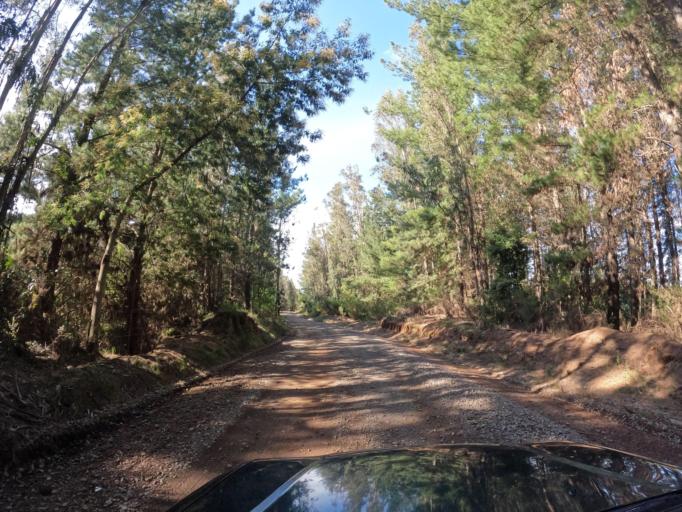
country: CL
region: Biobio
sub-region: Provincia de Biobio
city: La Laja
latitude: -37.0854
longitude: -72.7893
